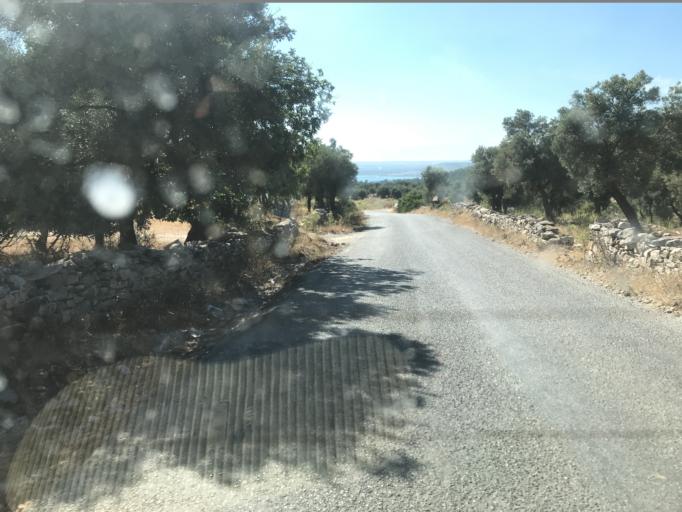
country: TR
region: Mugla
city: Selimiye
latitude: 37.3930
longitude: 27.4622
